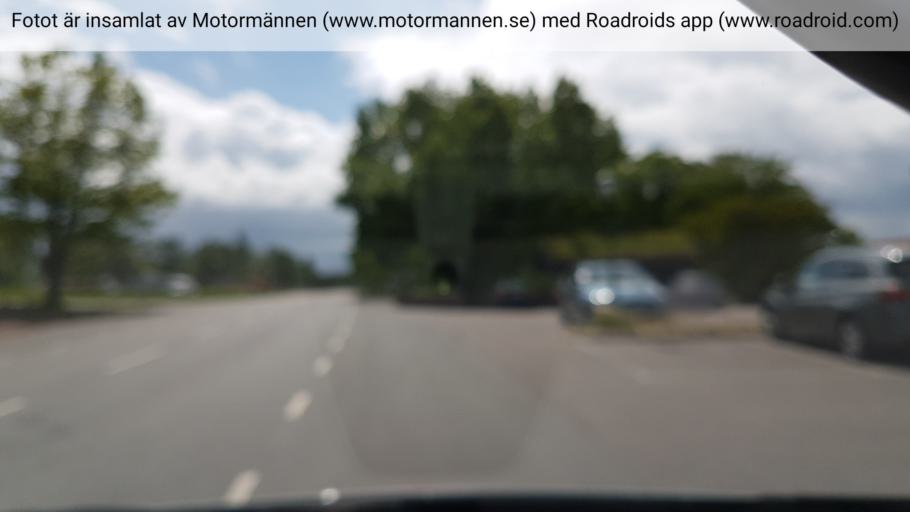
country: SE
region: Joenkoeping
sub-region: Jonkopings Kommun
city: Graenna
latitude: 57.9963
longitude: 14.4411
